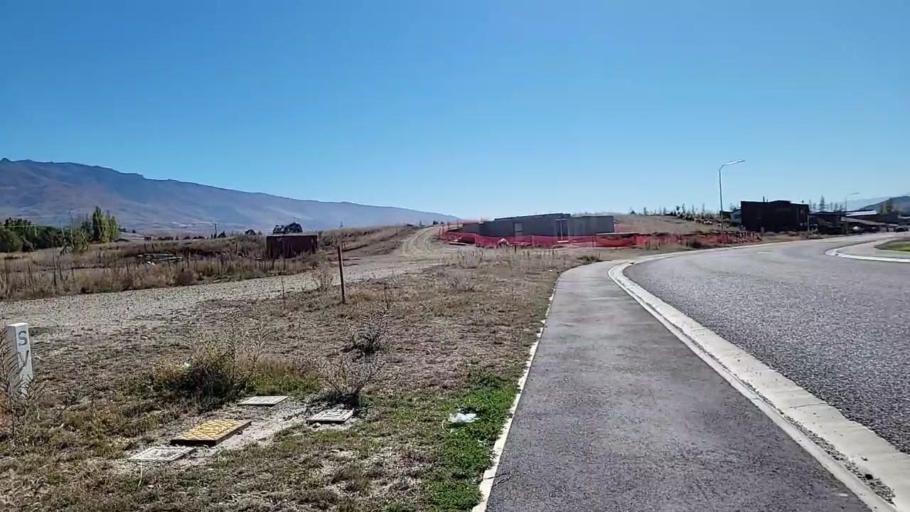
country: NZ
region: Otago
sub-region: Queenstown-Lakes District
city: Wanaka
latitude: -44.9765
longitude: 169.2375
